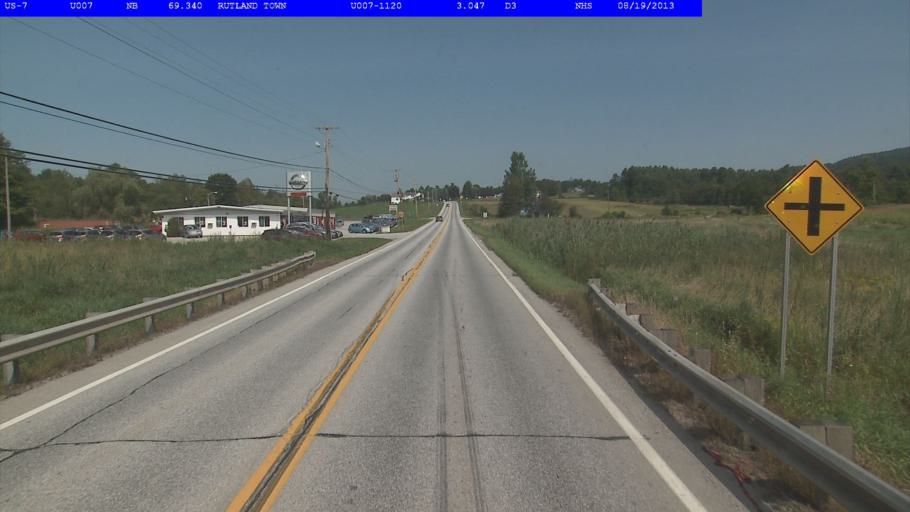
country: US
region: Vermont
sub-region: Rutland County
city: Rutland
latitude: 43.6545
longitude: -72.9868
